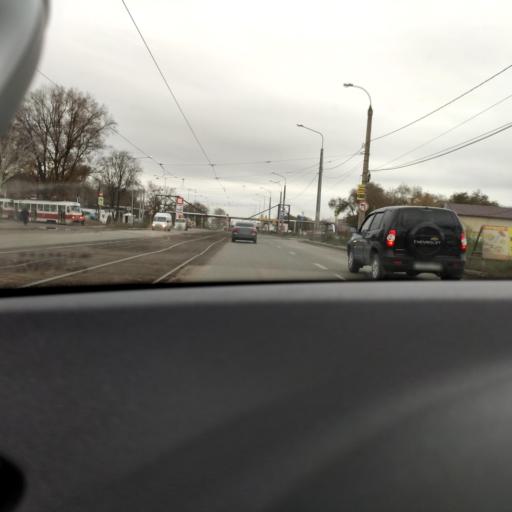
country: RU
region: Samara
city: Smyshlyayevka
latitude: 53.1935
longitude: 50.2929
